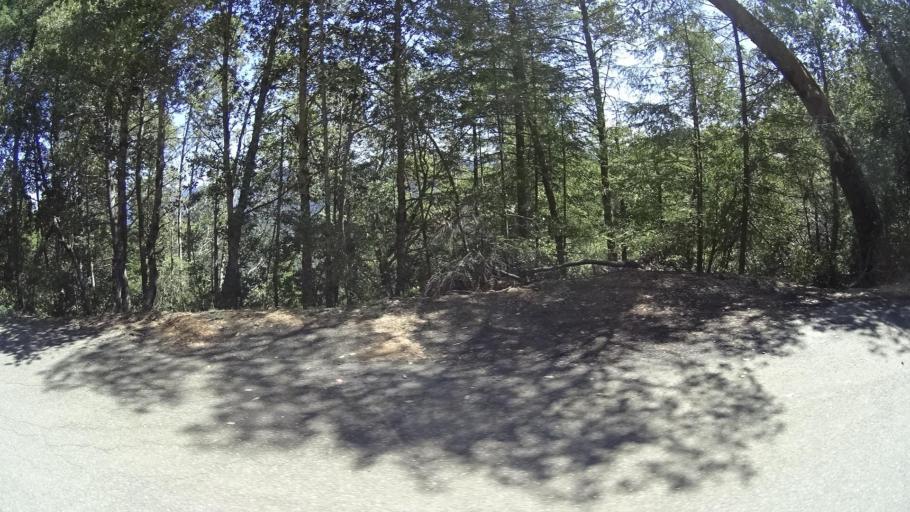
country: US
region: California
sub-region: Humboldt County
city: Redway
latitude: 40.1518
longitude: -124.0649
